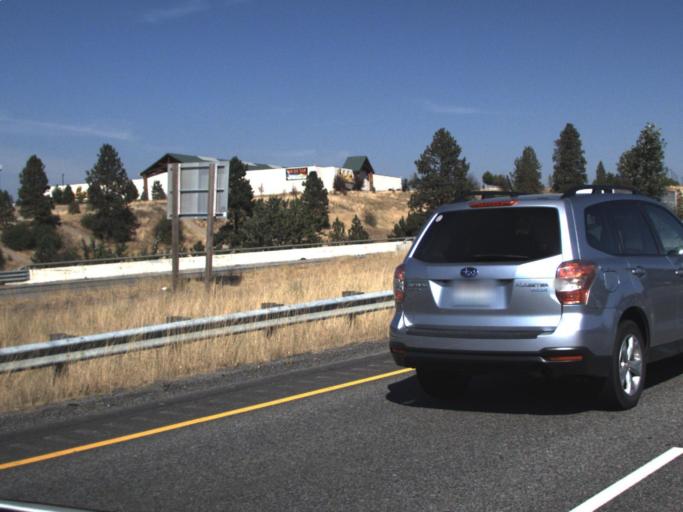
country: US
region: Washington
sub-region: Spokane County
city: Otis Orchards-East Farms
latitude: 47.6966
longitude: -117.0425
